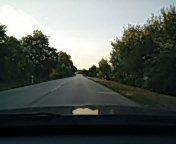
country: HU
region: Fejer
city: Etyek
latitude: 47.4995
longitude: 18.7604
